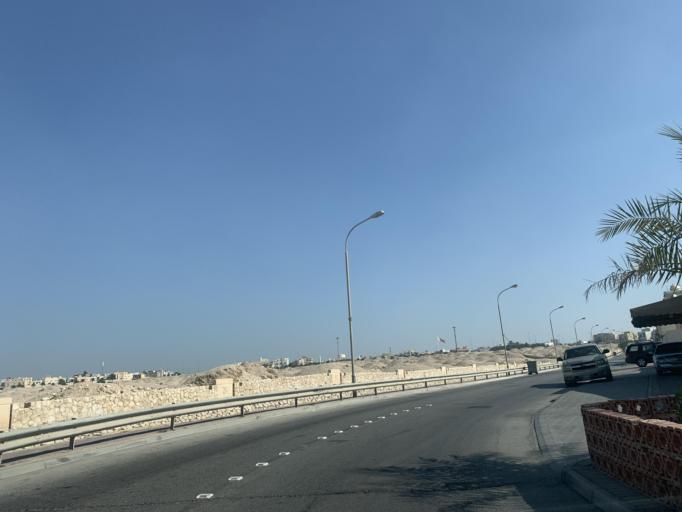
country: BH
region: Central Governorate
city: Madinat Hamad
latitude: 26.1183
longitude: 50.4966
